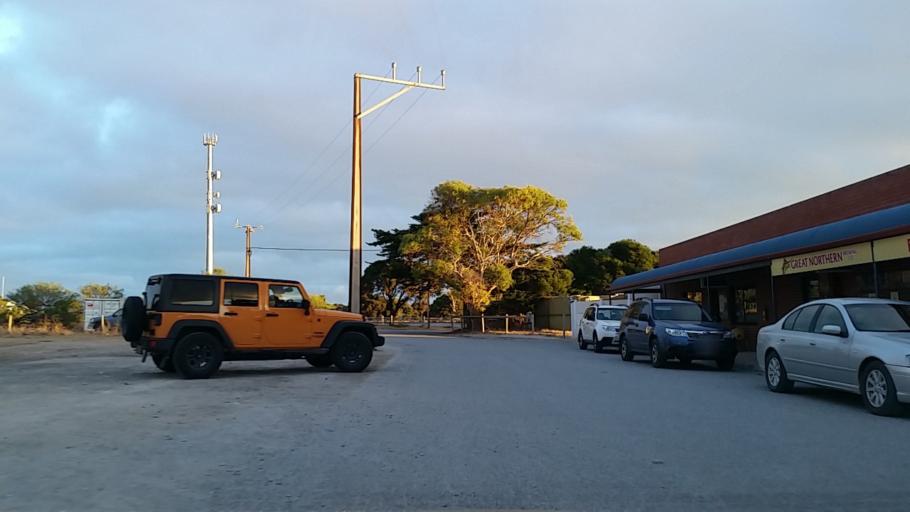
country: AU
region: South Australia
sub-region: Yankalilla
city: Normanville
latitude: -35.6042
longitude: 138.1082
